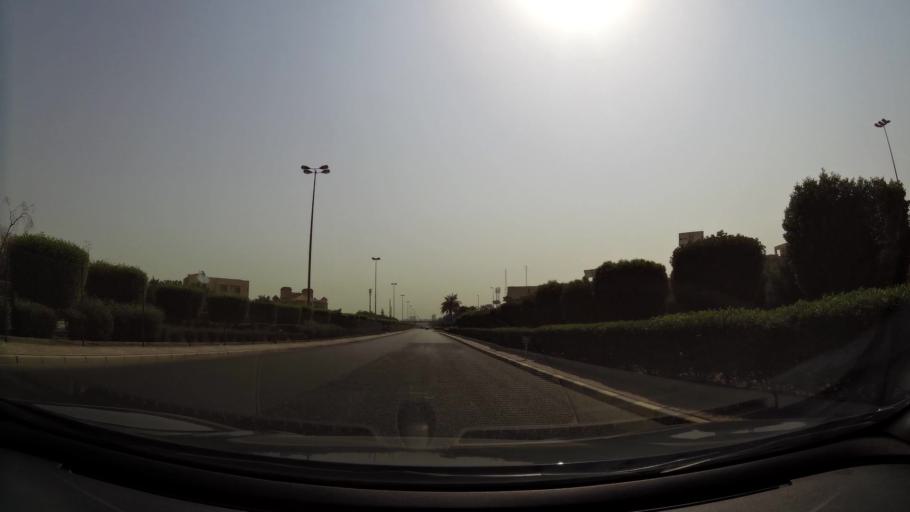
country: KW
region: Al Asimah
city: Ad Dasmah
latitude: 29.3621
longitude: 47.9959
